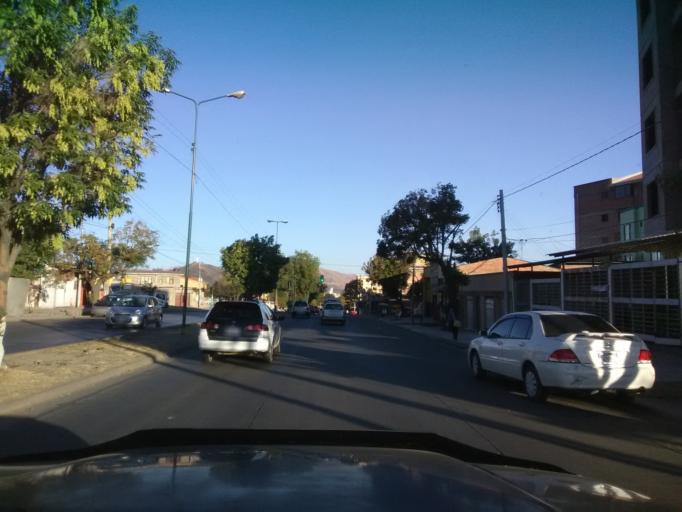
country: BO
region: Cochabamba
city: Cochabamba
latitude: -17.3601
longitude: -66.1712
